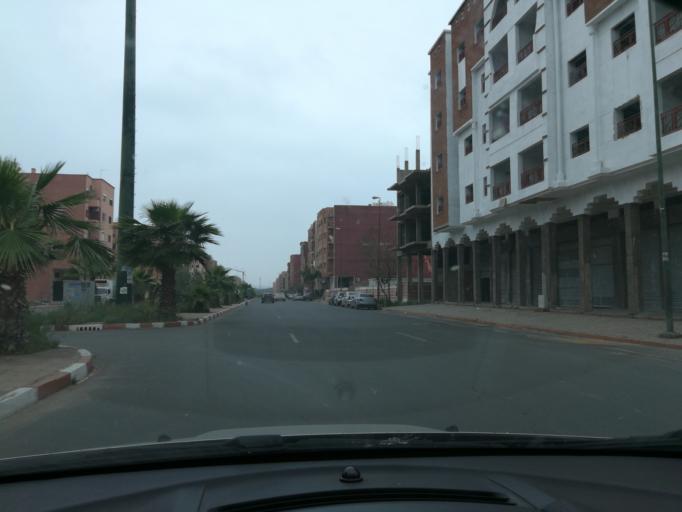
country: MA
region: Marrakech-Tensift-Al Haouz
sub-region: Marrakech
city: Marrakesh
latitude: 31.6718
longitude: -8.0277
